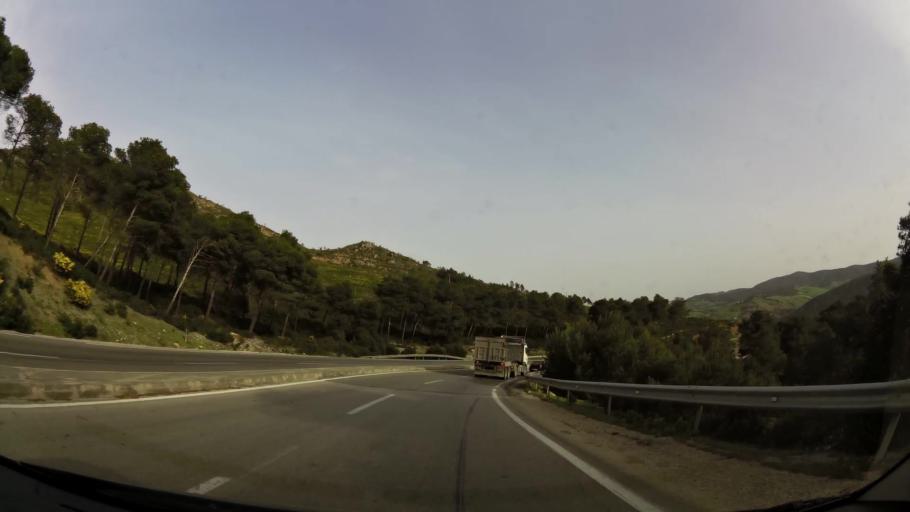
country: MA
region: Tanger-Tetouan
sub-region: Tetouan
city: Saddina
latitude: 35.5533
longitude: -5.5679
